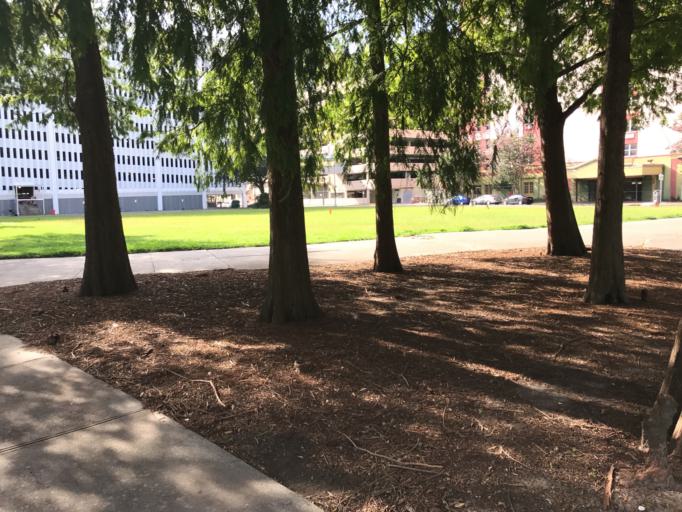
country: US
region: Louisiana
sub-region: Orleans Parish
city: New Orleans
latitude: 29.9533
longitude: -90.0762
